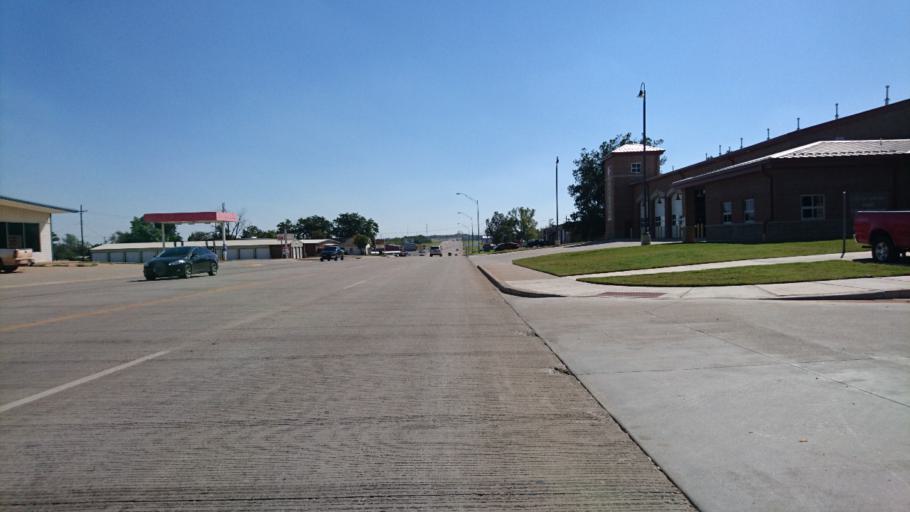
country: US
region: Oklahoma
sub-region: Custer County
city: Clinton
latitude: 35.5131
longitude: -98.9649
